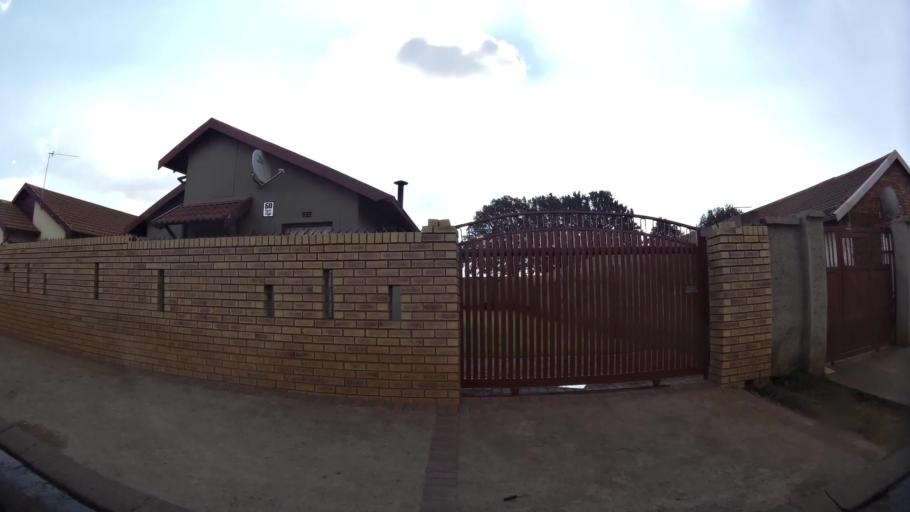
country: ZA
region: Gauteng
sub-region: City of Johannesburg Metropolitan Municipality
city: Roodepoort
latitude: -26.2113
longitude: 27.8662
